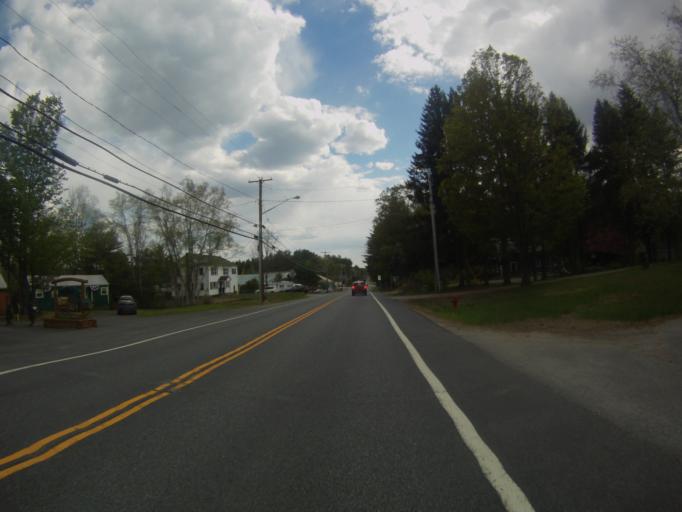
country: US
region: New York
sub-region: Essex County
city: Ticonderoga
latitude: 43.8533
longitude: -73.7568
